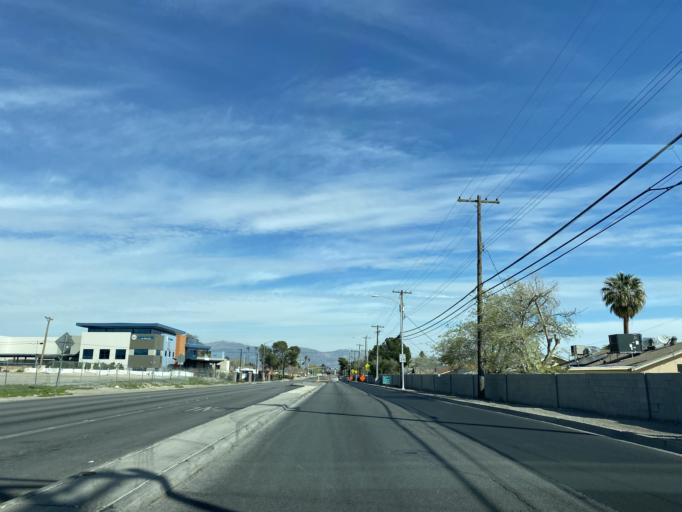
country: US
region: Nevada
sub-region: Clark County
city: Las Vegas
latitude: 36.1813
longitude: -115.1250
